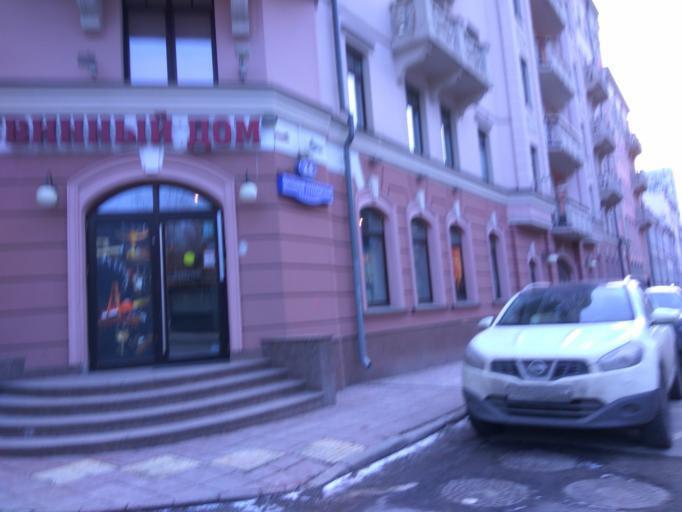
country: RU
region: Moscow
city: Moscow
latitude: 55.7708
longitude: 37.6306
